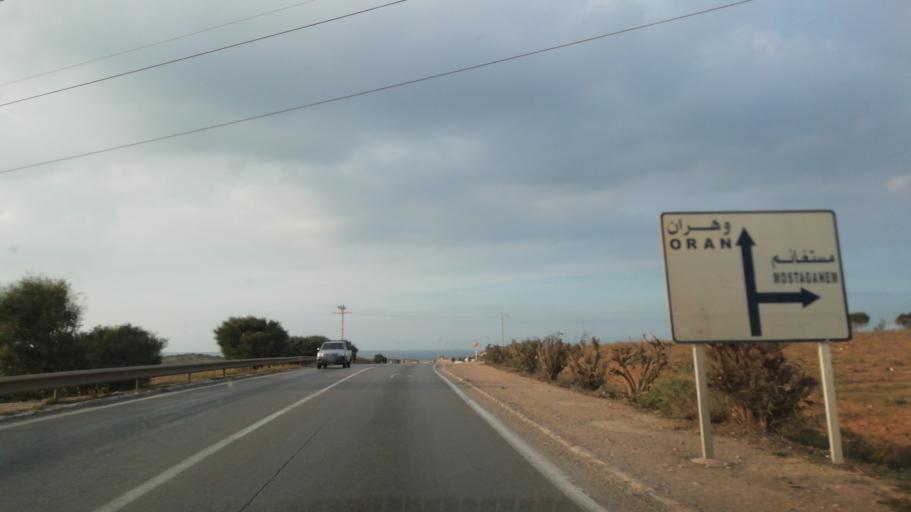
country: DZ
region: Oran
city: Ain el Bya
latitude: 35.7844
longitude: -0.1010
